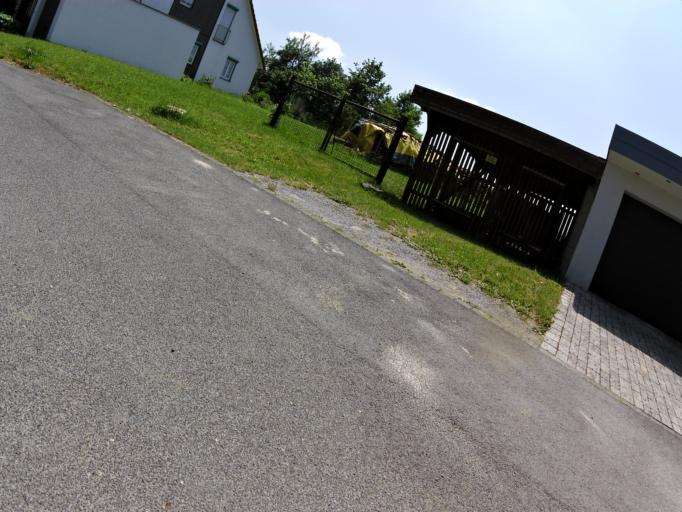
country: DE
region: Bavaria
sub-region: Regierungsbezirk Unterfranken
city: Kleinrinderfeld
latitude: 49.6955
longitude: 9.8439
